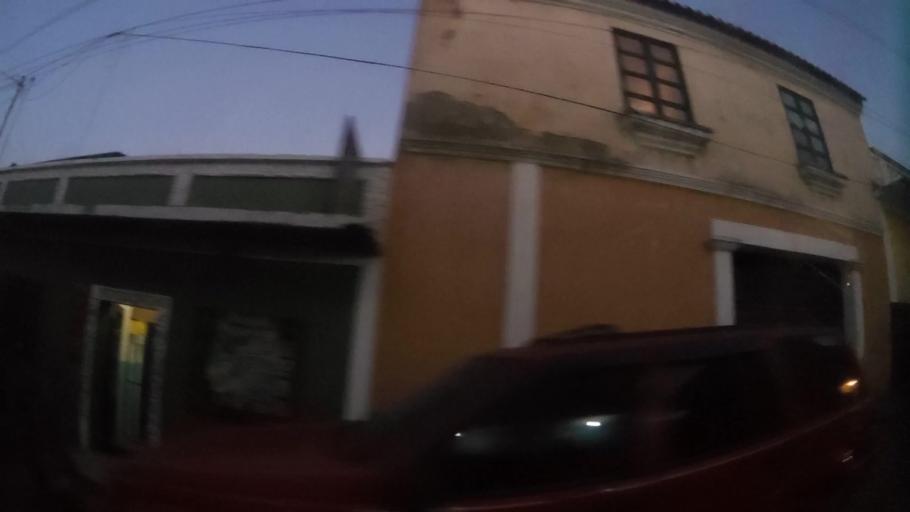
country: GT
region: Sacatepequez
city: Ciudad Vieja
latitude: 14.5248
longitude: -90.7599
